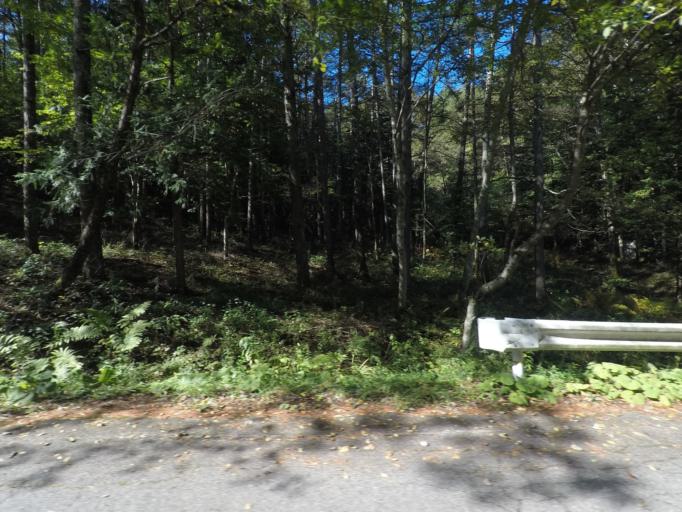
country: JP
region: Nagano
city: Tatsuno
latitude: 35.9714
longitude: 137.7437
